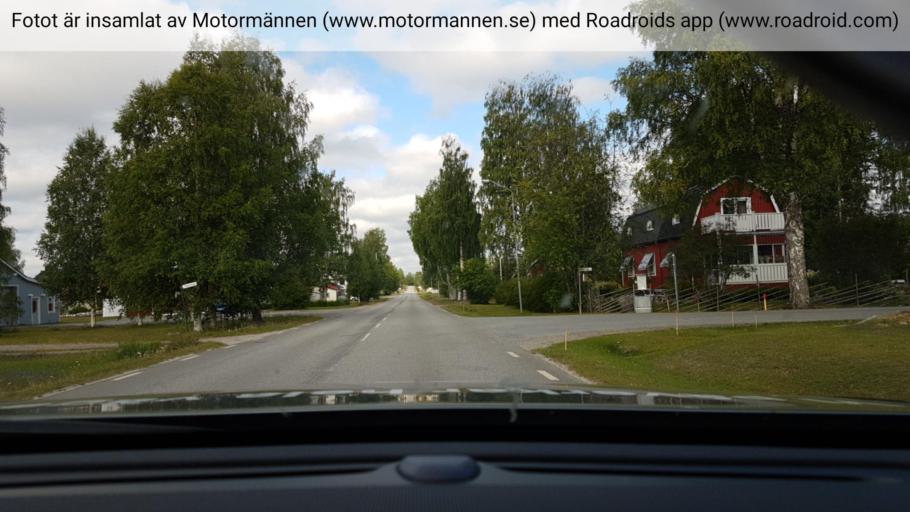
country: SE
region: Vaesterbotten
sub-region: Lycksele Kommun
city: Lycksele
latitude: 64.8134
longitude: 18.9047
